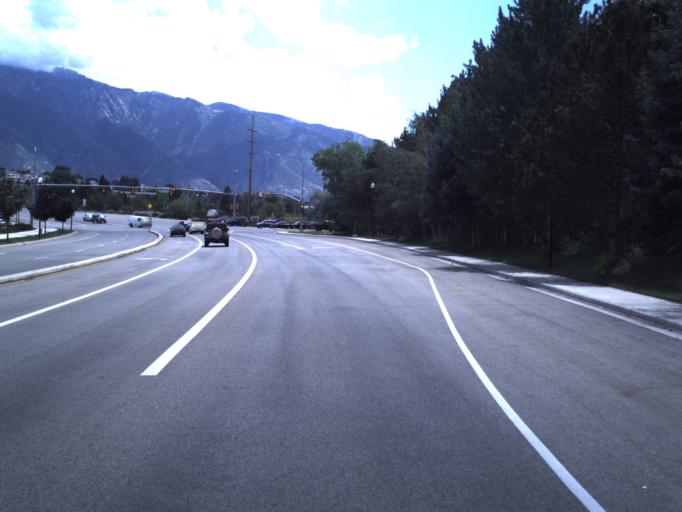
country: US
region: Utah
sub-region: Salt Lake County
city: Sandy Hills
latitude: 40.5821
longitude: -111.8628
